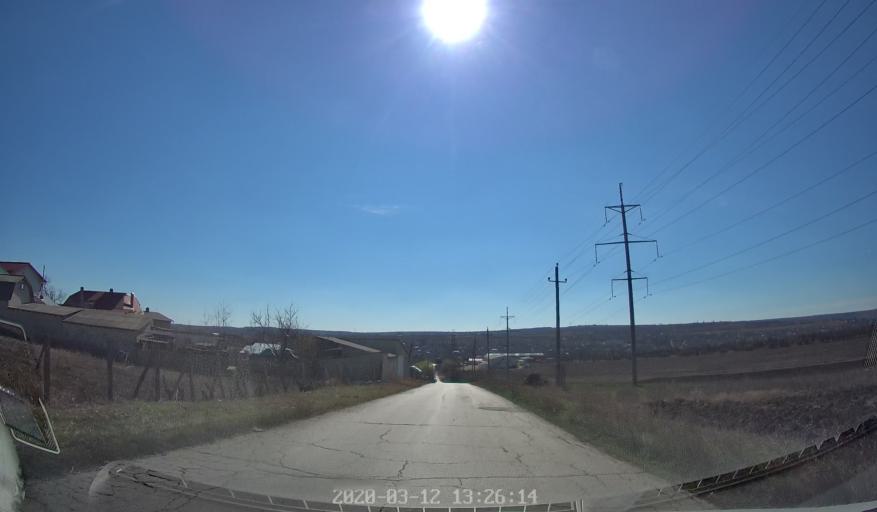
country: MD
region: Laloveni
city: Ialoveni
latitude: 46.9362
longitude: 28.8158
